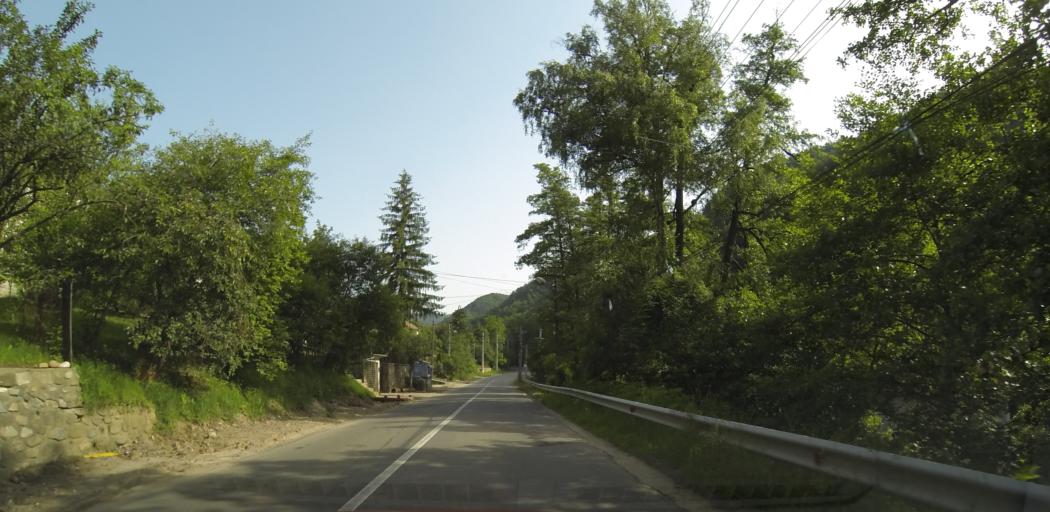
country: RO
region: Valcea
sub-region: Oras Baile Olanesti
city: Olanesti
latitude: 45.1903
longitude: 24.2518
